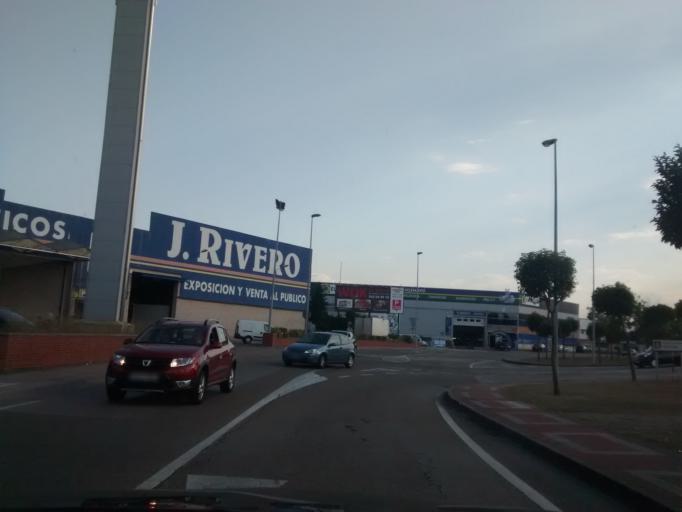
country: ES
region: Cantabria
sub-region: Provincia de Cantabria
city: El Astillero
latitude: 43.4249
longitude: -3.8365
